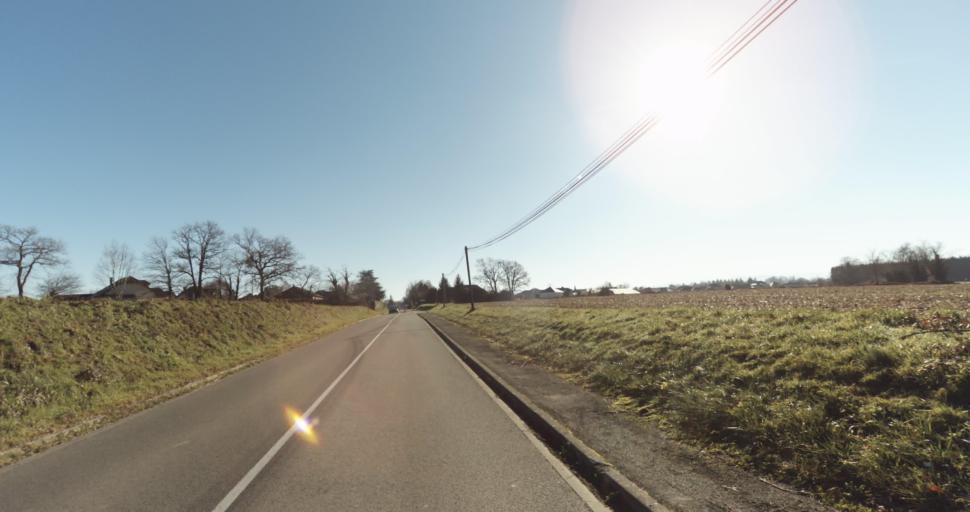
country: FR
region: Aquitaine
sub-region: Departement des Pyrenees-Atlantiques
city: Morlaas
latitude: 43.3534
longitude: -0.2678
